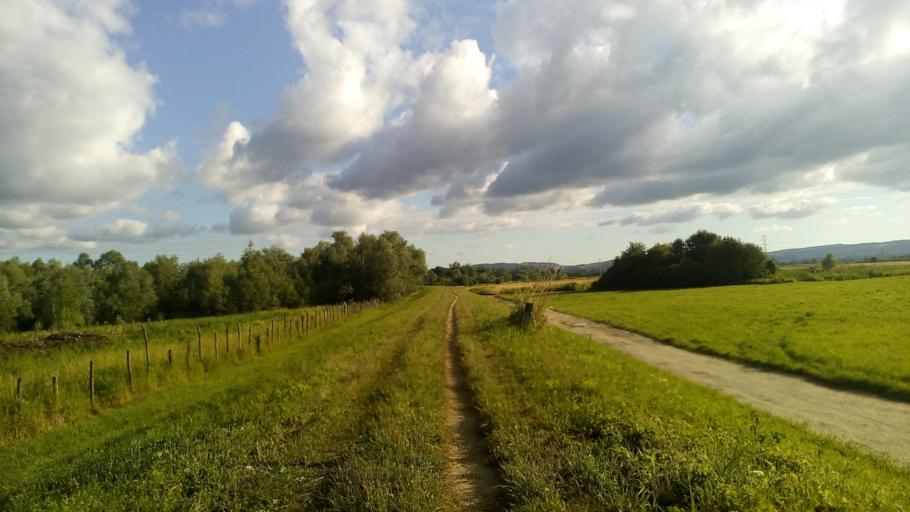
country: PL
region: Lesser Poland Voivodeship
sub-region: Powiat nowosadecki
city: Stary Sacz
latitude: 49.5821
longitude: 20.6537
